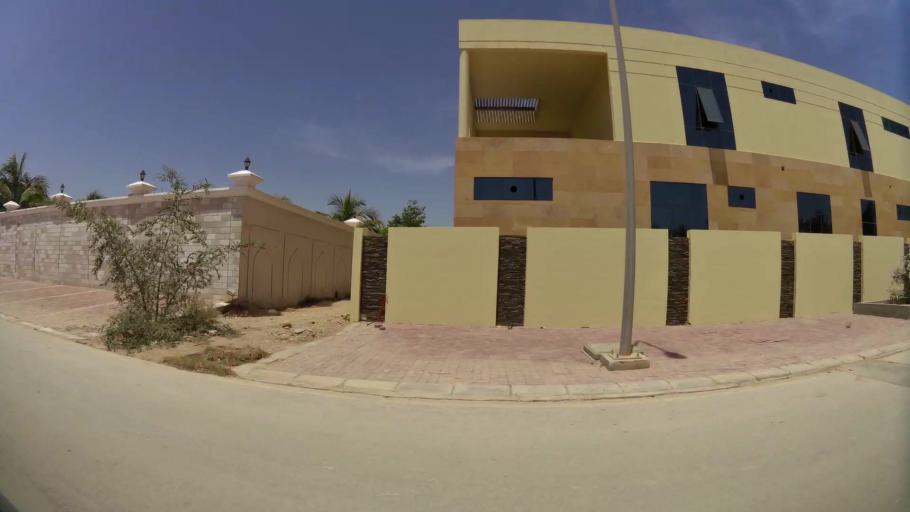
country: OM
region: Zufar
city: Salalah
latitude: 17.0647
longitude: 54.1479
